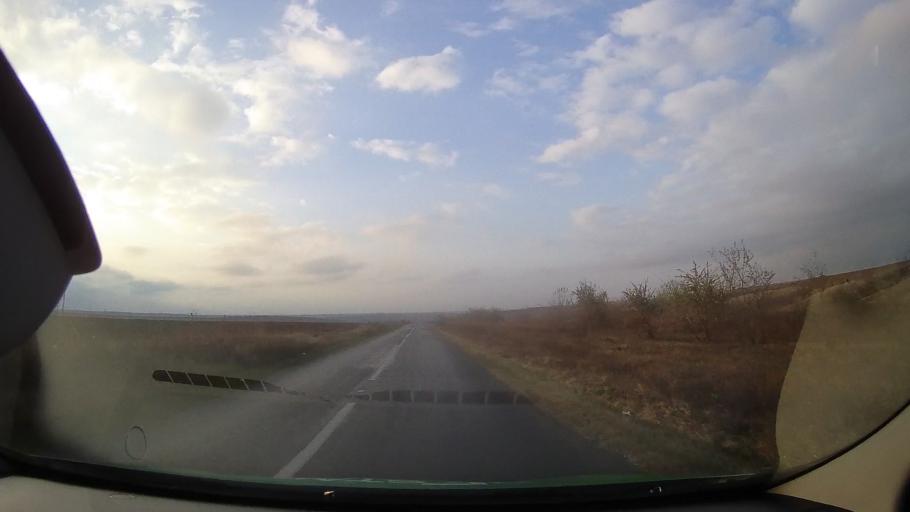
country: RO
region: Constanta
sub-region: Comuna Adamclisi
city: Adamclisi
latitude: 44.0178
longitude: 27.8906
